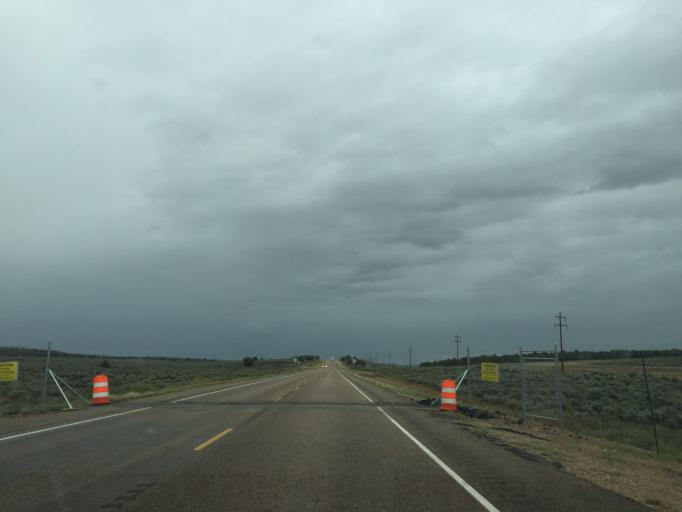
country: US
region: Utah
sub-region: Kane County
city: Kanab
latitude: 37.1401
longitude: -112.0770
